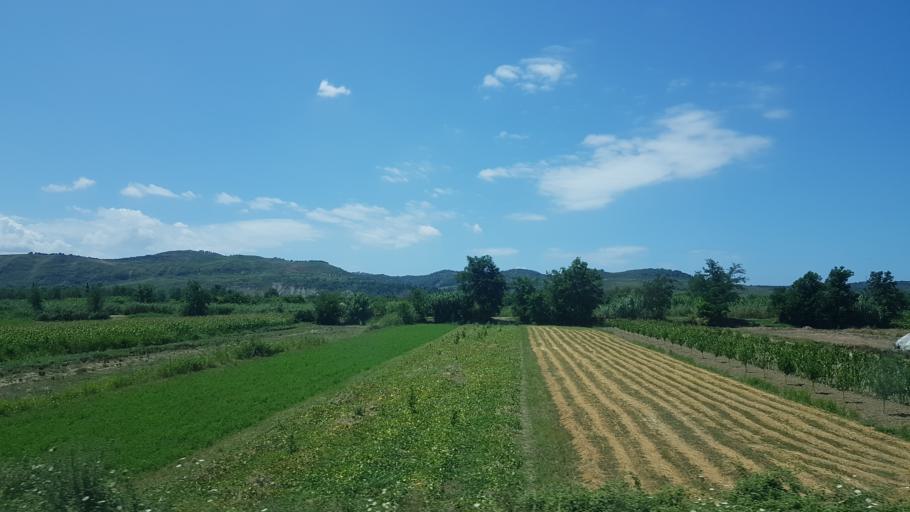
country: AL
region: Fier
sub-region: Rrethi i Fierit
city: Frakulla e Madhe
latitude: 40.6106
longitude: 19.5272
